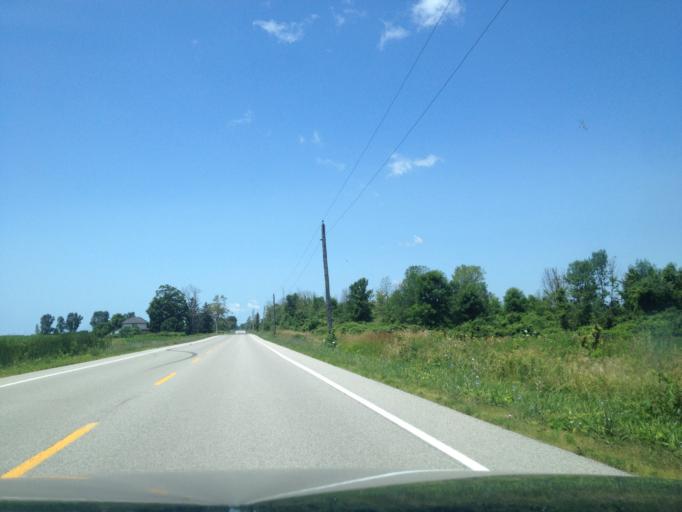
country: CA
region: Ontario
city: Norfolk County
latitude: 42.5778
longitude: -80.5567
